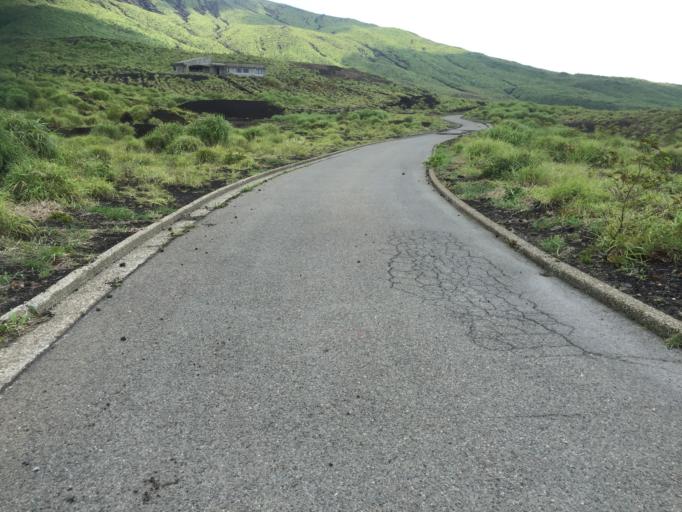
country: JP
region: Shizuoka
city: Shimoda
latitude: 34.0714
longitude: 139.5132
